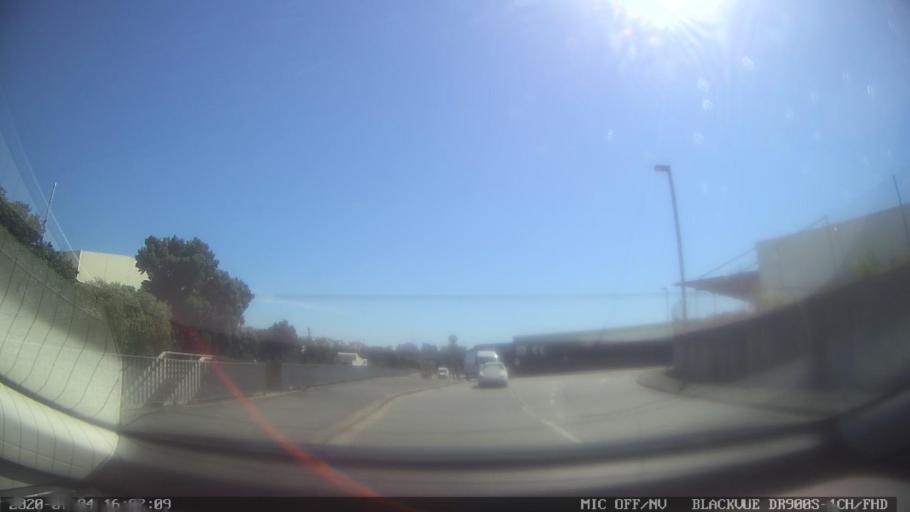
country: PT
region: Porto
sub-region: Maia
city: Maia
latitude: 41.2440
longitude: -8.6251
